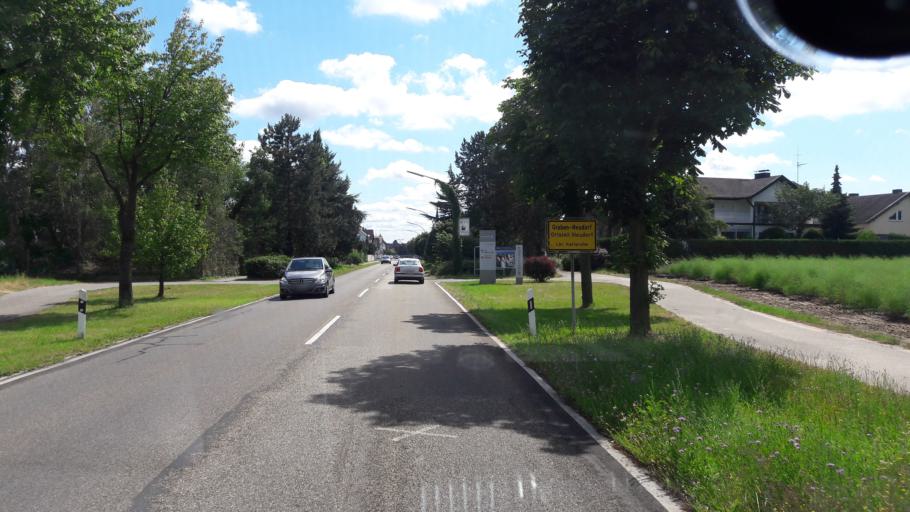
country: DE
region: Baden-Wuerttemberg
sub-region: Karlsruhe Region
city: Graben-Neudorf
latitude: 49.1795
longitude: 8.4996
